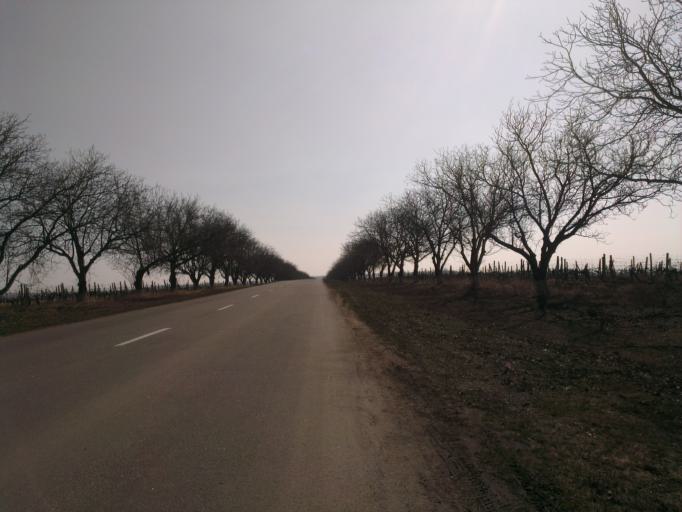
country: MD
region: Chisinau
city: Cricova
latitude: 47.1274
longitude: 28.8547
